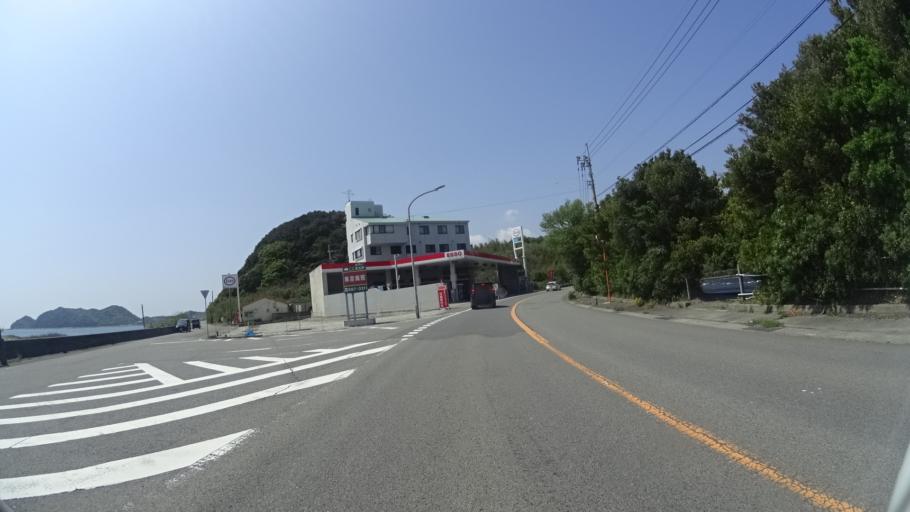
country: JP
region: Tokushima
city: Narutocho-mitsuishi
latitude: 34.1962
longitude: 134.6254
